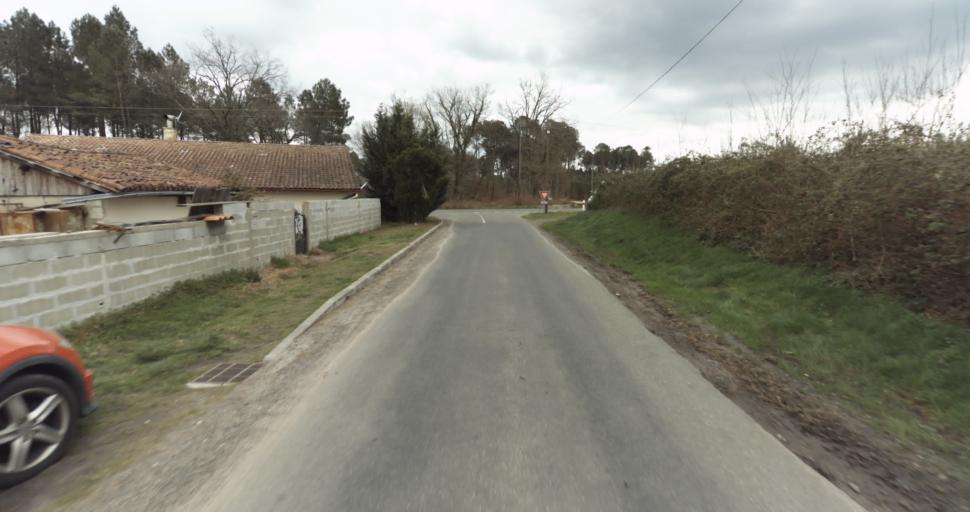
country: FR
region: Aquitaine
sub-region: Departement des Landes
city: Sarbazan
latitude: 44.0097
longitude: -0.3244
